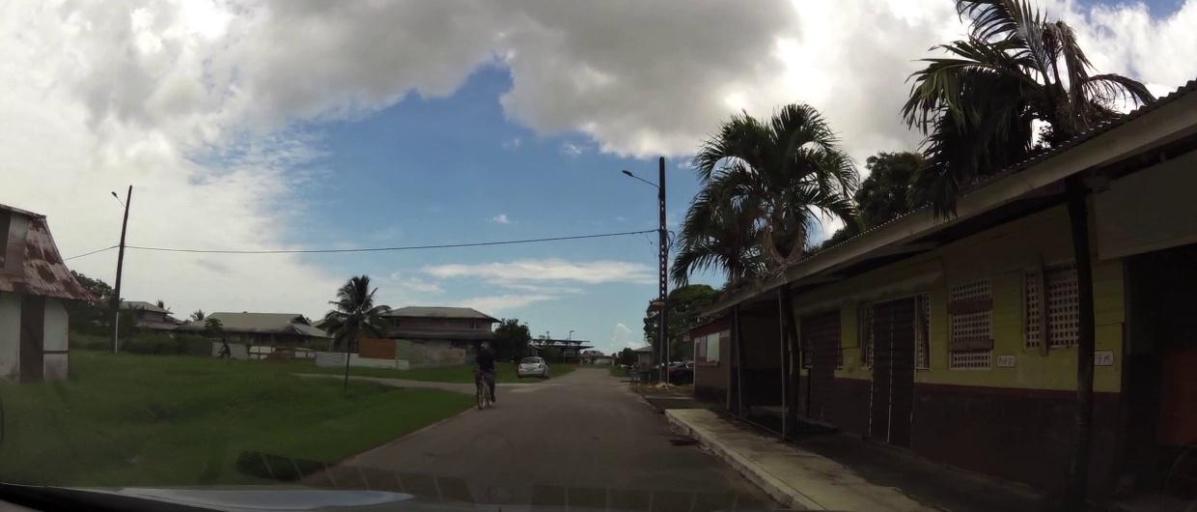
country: GF
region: Guyane
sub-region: Guyane
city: Sinnamary
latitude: 5.3753
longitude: -52.9554
